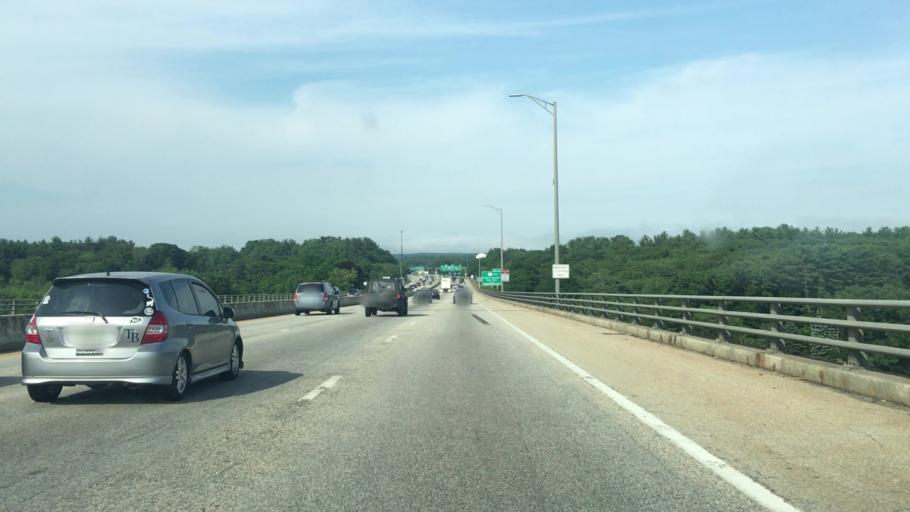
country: US
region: Maine
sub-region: York County
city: South Eliot
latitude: 43.0946
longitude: -70.7628
